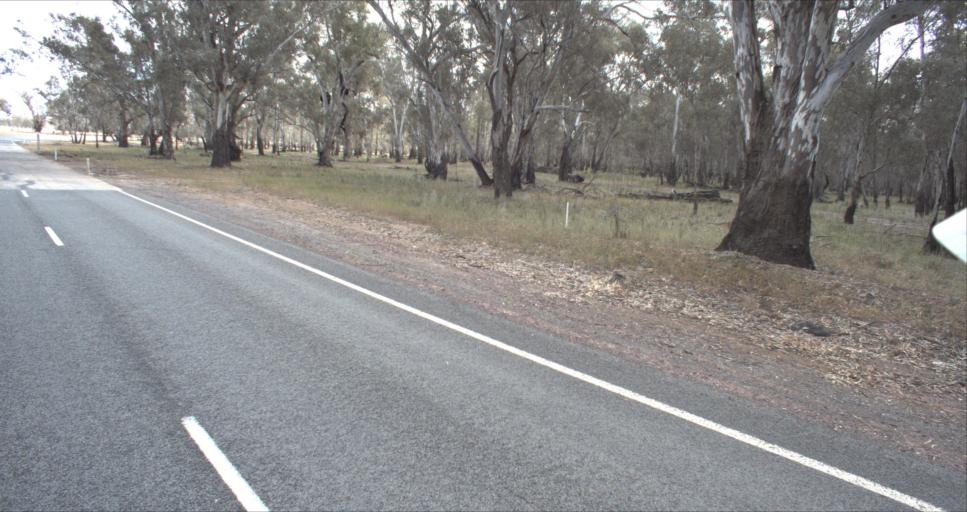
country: AU
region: New South Wales
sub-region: Leeton
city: Leeton
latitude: -34.6421
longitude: 146.3580
